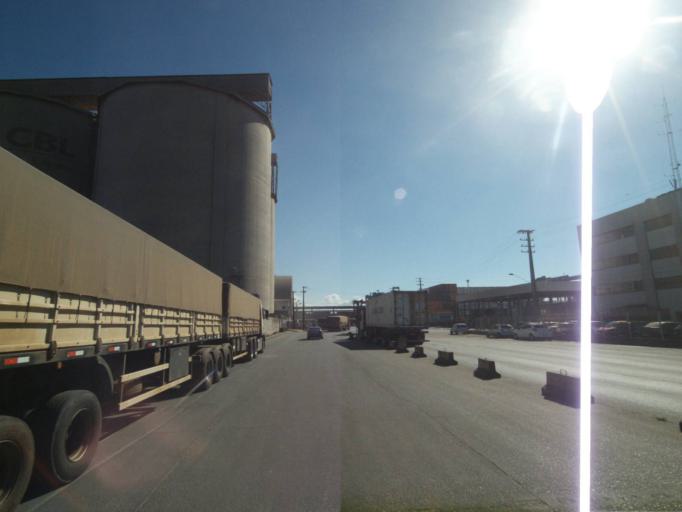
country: BR
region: Parana
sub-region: Paranagua
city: Paranagua
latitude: -25.5051
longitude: -48.5041
